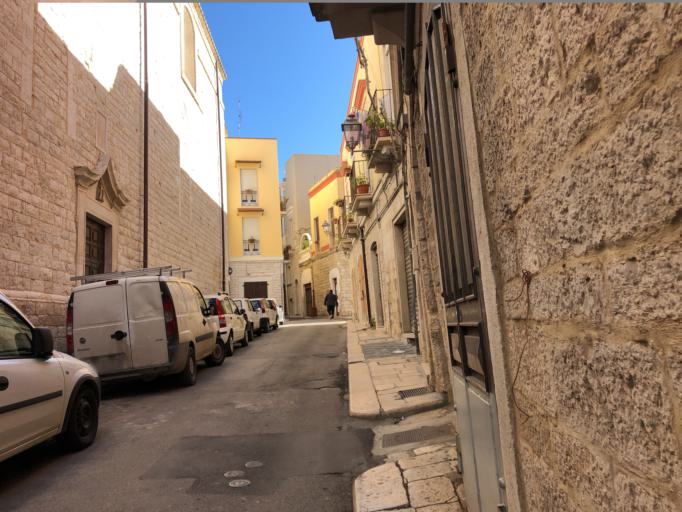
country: IT
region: Apulia
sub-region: Provincia di Barletta - Andria - Trani
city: Andria
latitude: 41.2250
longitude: 16.2937
